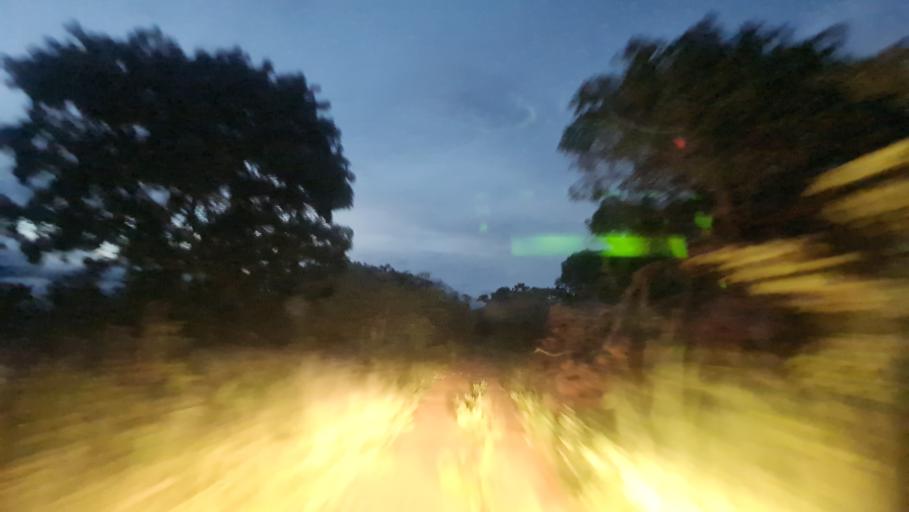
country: MZ
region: Nampula
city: Nampula
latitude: -14.6817
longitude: 39.8329
